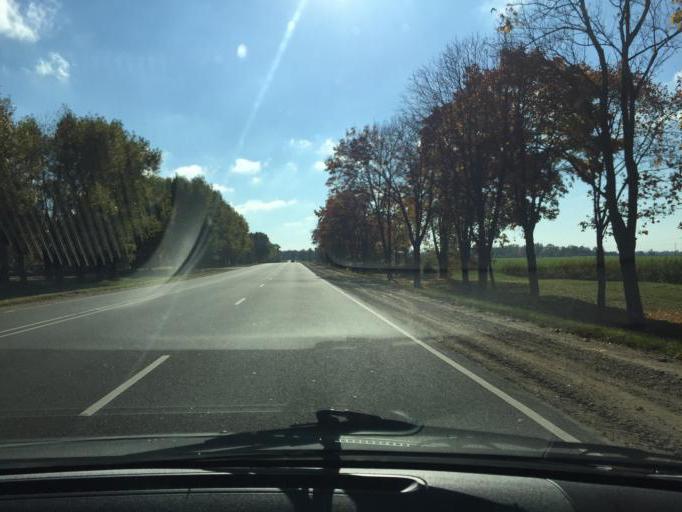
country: BY
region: Minsk
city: Slutsk
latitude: 53.0642
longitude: 27.5536
